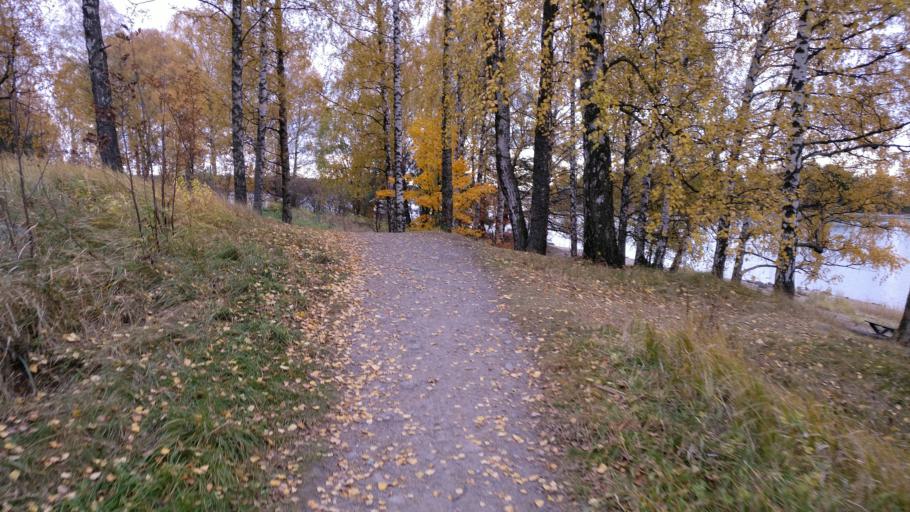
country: FI
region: Uusimaa
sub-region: Helsinki
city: Helsinki
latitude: 60.1787
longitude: 24.9886
